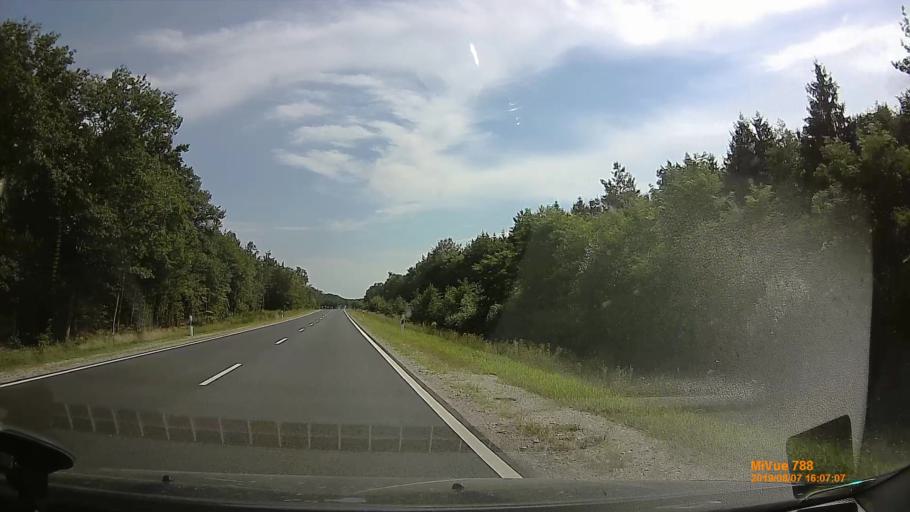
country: HU
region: Zala
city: Zalalovo
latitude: 46.9261
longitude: 16.6002
